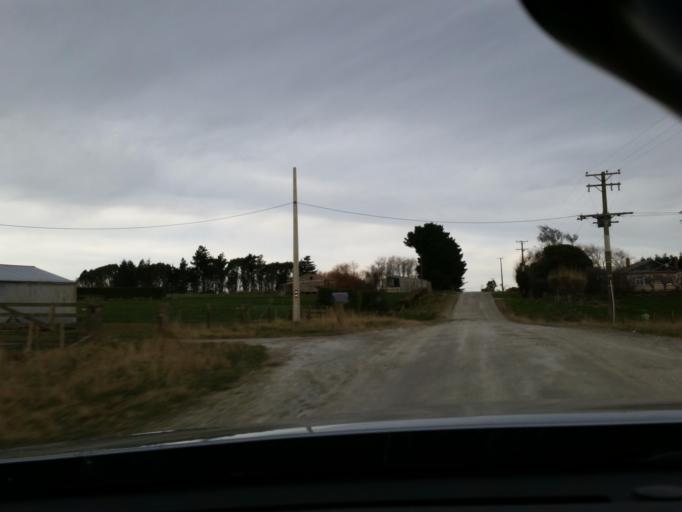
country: NZ
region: Southland
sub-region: Invercargill City
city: Invercargill
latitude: -46.4159
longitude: 168.5061
